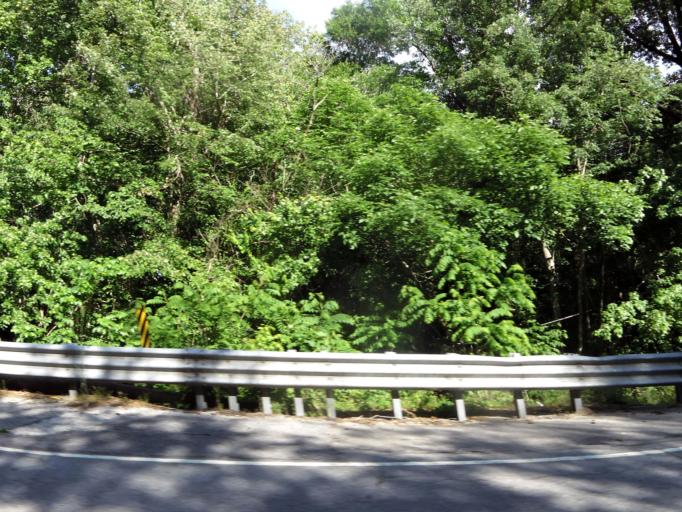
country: US
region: South Carolina
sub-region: Allendale County
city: Fairfax
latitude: 33.0548
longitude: -81.2173
